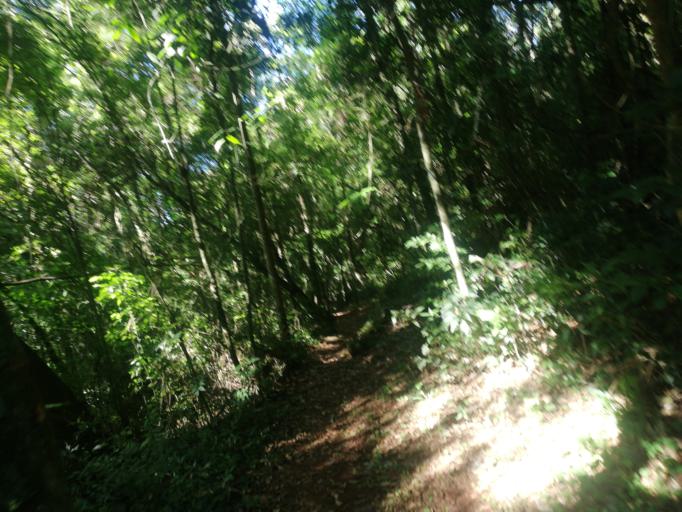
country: AR
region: Misiones
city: Cerro Azul
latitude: -27.7531
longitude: -55.5608
